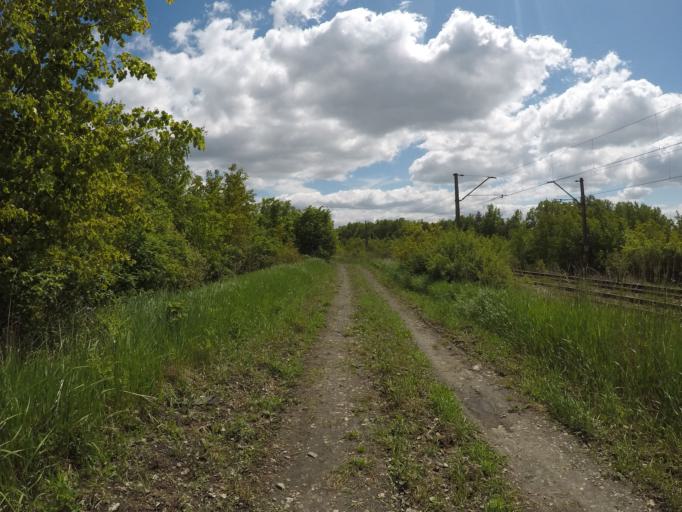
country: PL
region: Swietokrzyskie
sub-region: Powiat kielecki
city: Kostomloty Pierwsze
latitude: 50.9273
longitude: 20.6044
